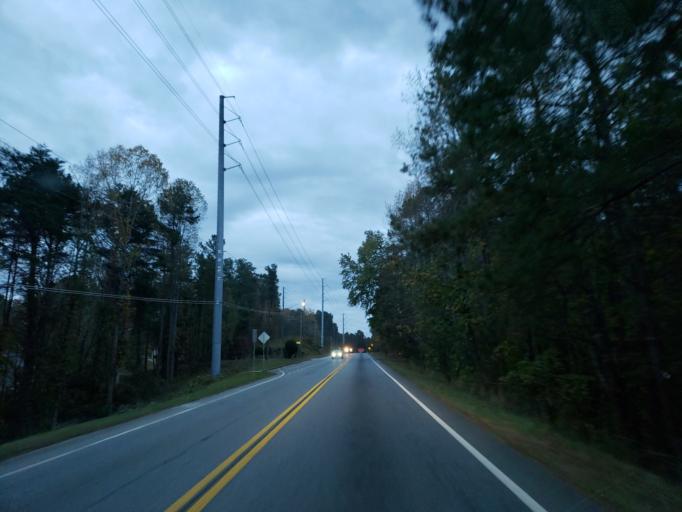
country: US
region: Georgia
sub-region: Paulding County
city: Hiram
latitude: 33.9536
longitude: -84.7383
